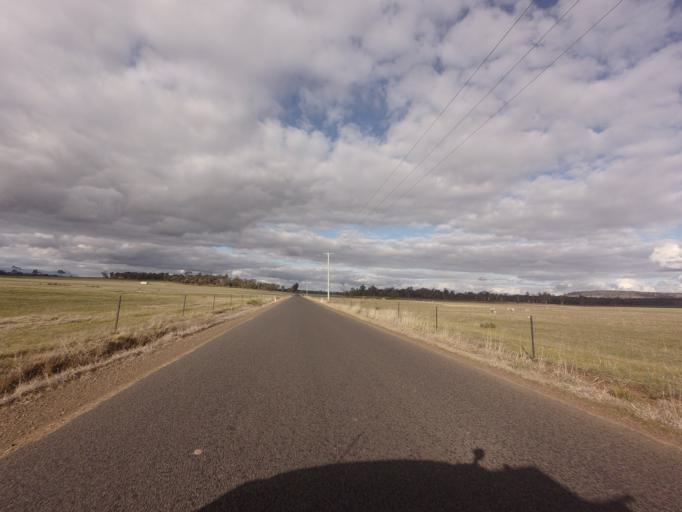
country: AU
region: Tasmania
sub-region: Northern Midlands
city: Longford
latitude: -41.8614
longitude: 147.2543
